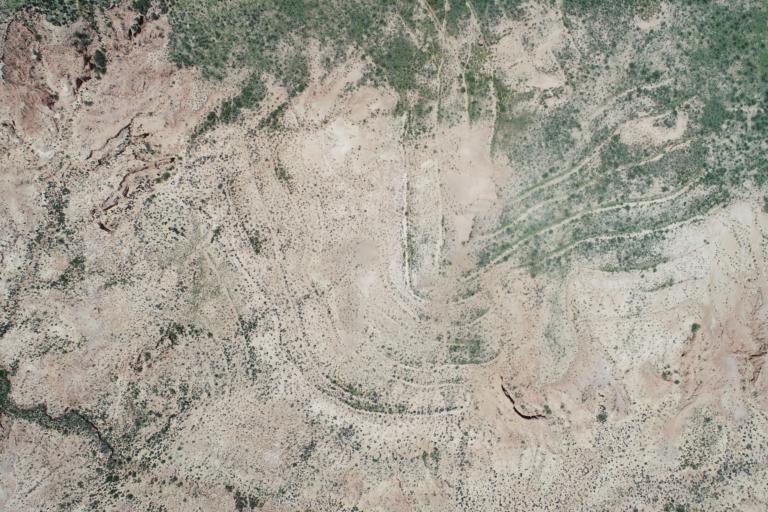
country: BO
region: La Paz
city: Curahuara de Carangas
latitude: -17.3285
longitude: -68.5097
